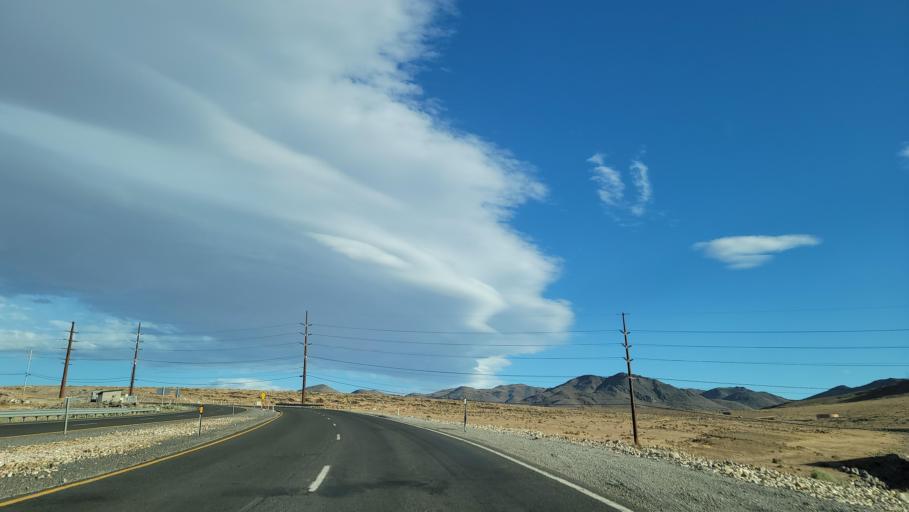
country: US
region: Nevada
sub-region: Lyon County
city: Stagecoach
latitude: 39.5519
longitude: -119.4908
